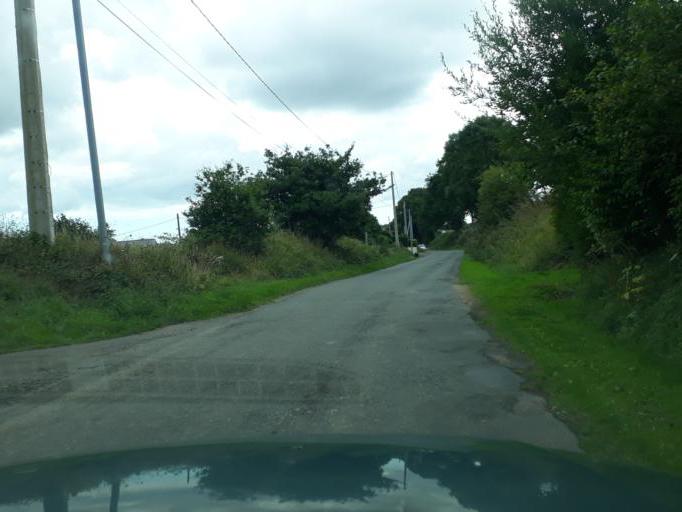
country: FR
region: Brittany
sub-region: Departement des Cotes-d'Armor
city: Plehedel
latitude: 48.6750
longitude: -2.9941
